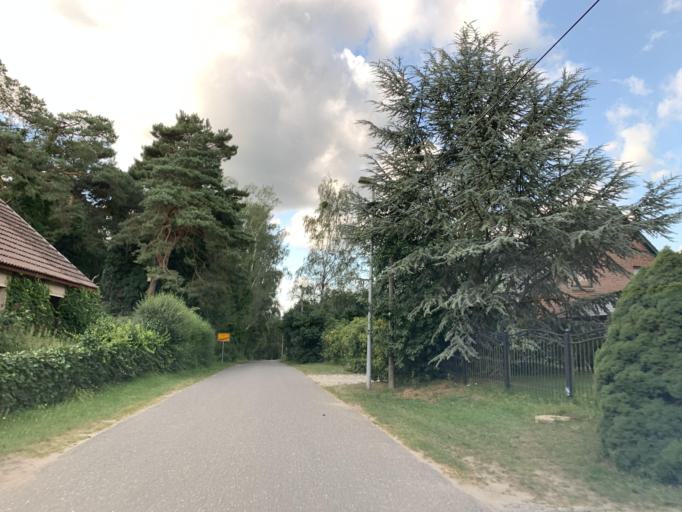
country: DE
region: Mecklenburg-Vorpommern
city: Carpin
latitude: 53.3657
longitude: 13.2406
